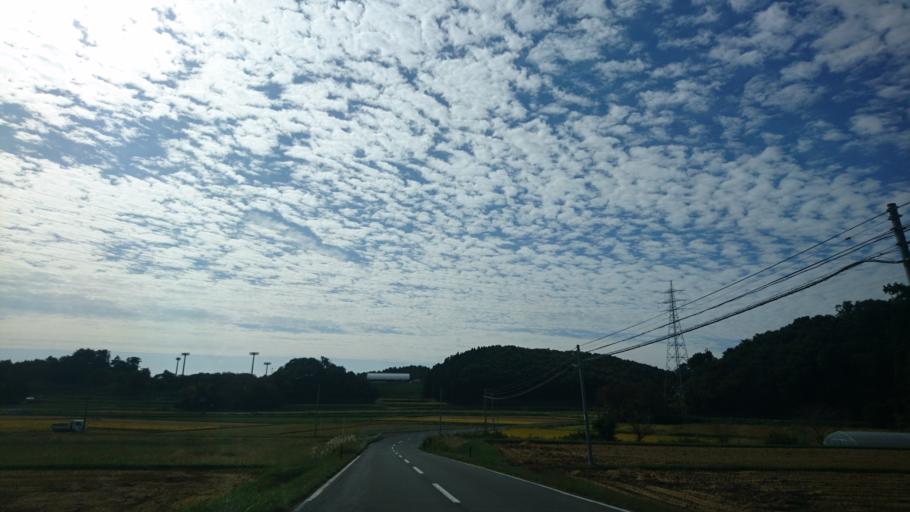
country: JP
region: Fukushima
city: Sukagawa
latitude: 37.3130
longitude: 140.2676
